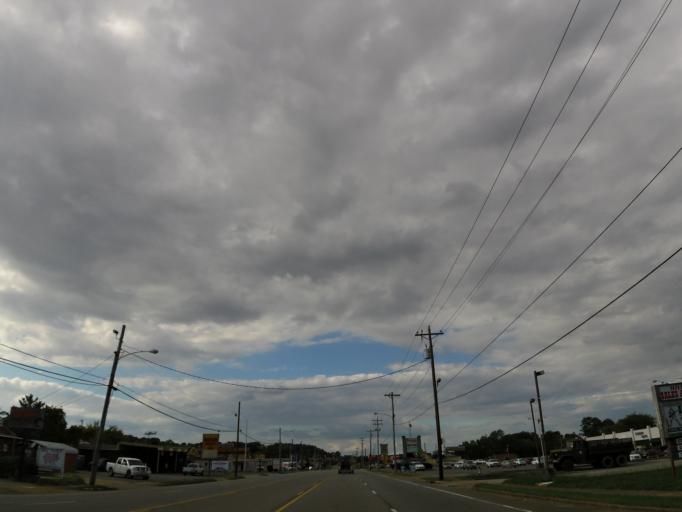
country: US
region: Georgia
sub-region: Catoosa County
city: Fort Oglethorpe
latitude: 34.9461
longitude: -85.2588
